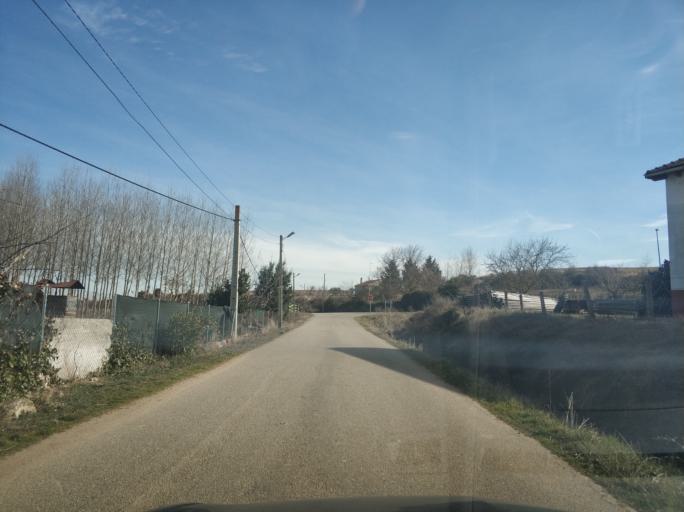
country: ES
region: Castille and Leon
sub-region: Provincia de Salamanca
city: Valverdon
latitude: 41.0389
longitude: -5.7889
